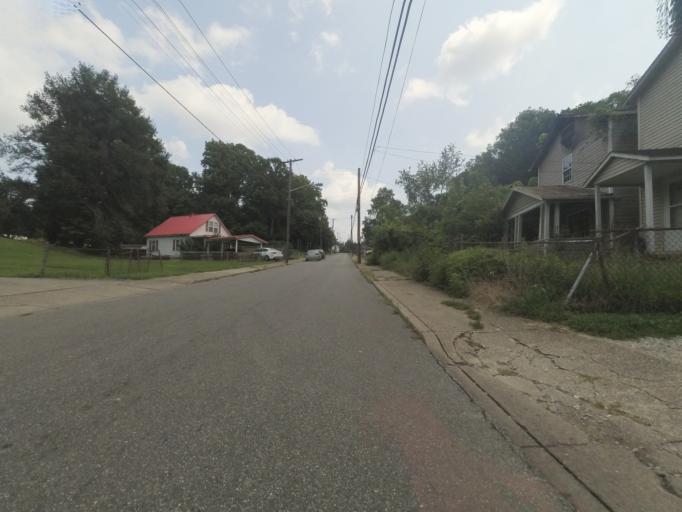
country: US
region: West Virginia
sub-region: Cabell County
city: Huntington
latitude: 38.4162
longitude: -82.4047
